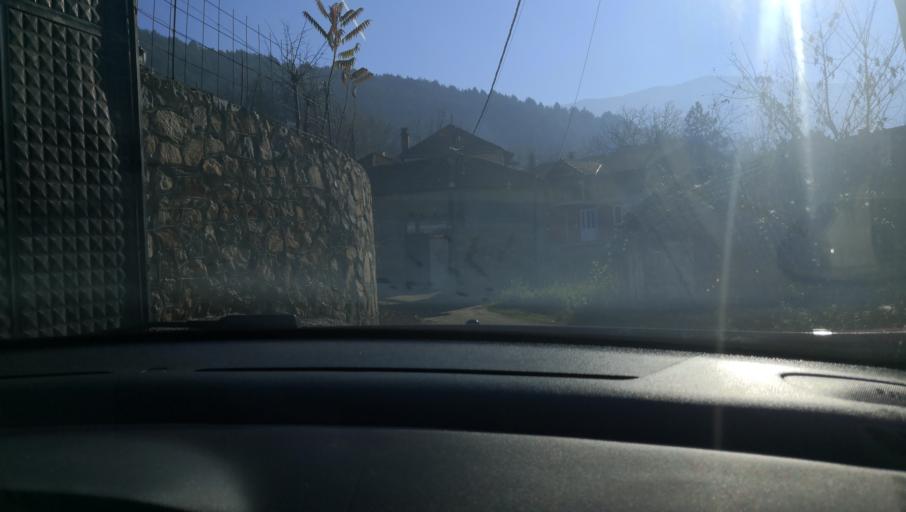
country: MK
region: Brvenica
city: Celopek
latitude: 41.9248
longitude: 21.0215
